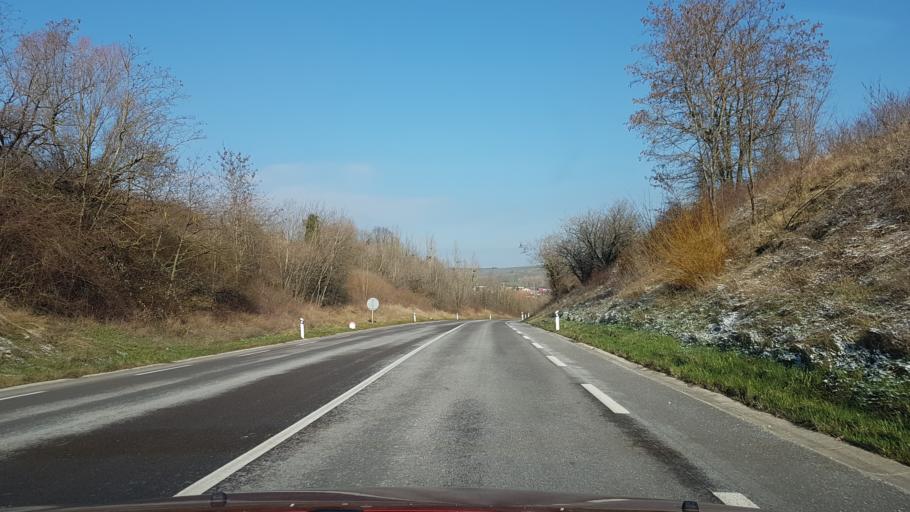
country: FR
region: Franche-Comte
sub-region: Departement du Jura
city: Arbois
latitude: 46.9071
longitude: 5.7649
